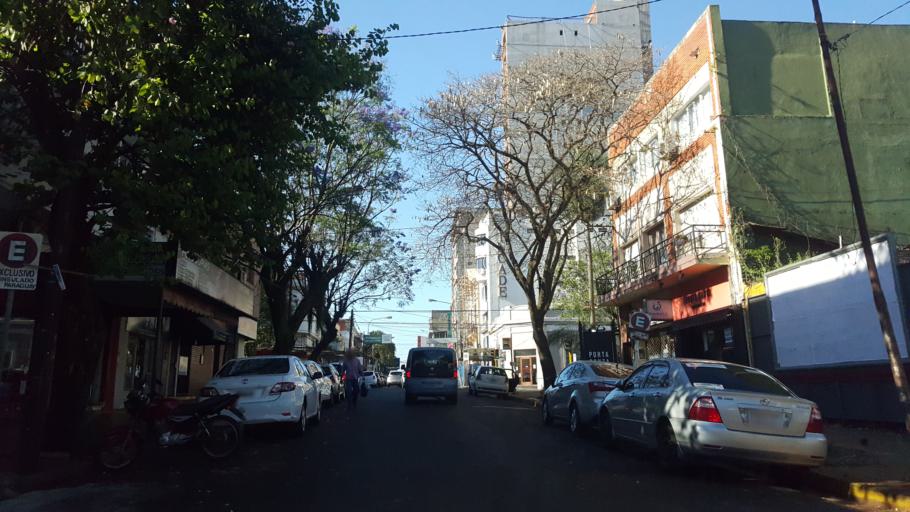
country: AR
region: Misiones
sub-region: Departamento de Capital
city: Posadas
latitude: -27.3644
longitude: -55.8954
